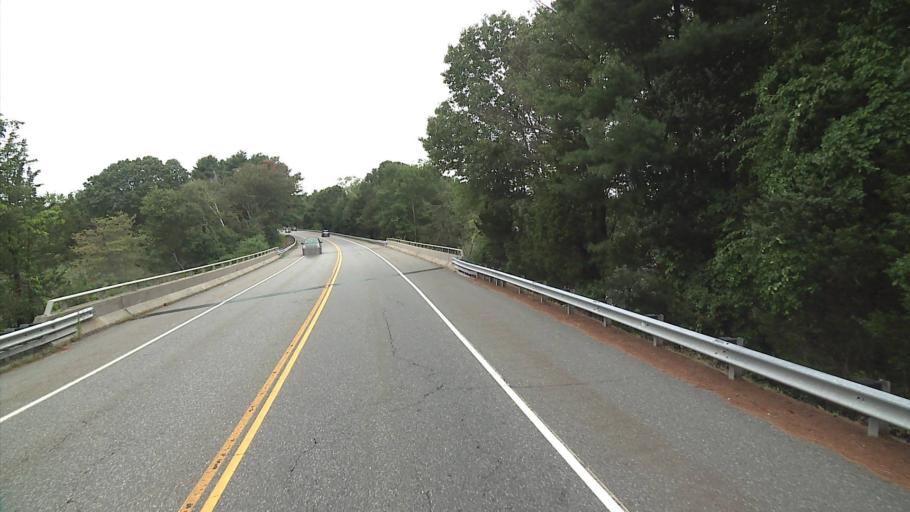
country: US
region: Connecticut
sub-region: Middlesex County
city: Old Saybrook Center
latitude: 41.3061
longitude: -72.3299
